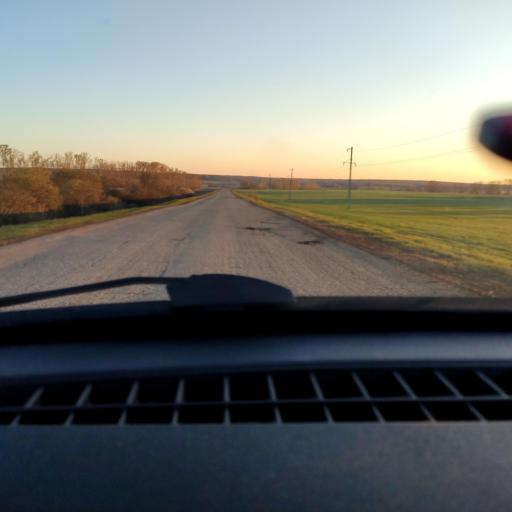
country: RU
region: Bashkortostan
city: Chishmy
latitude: 54.4628
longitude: 55.5407
